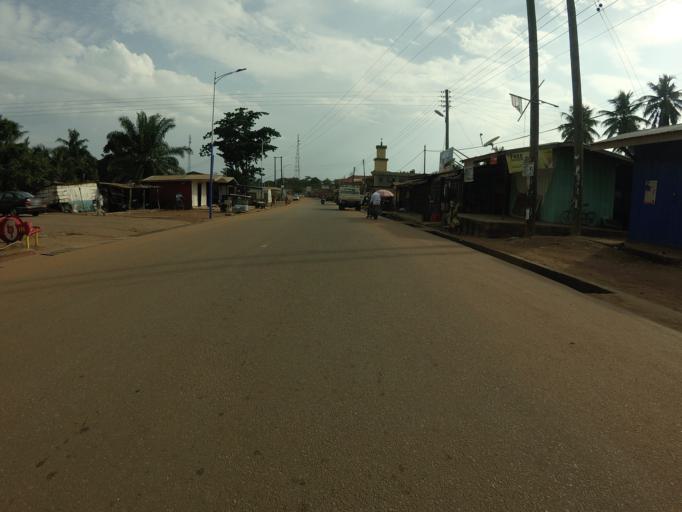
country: GH
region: Volta
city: Hohoe
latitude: 7.1496
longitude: 0.4688
